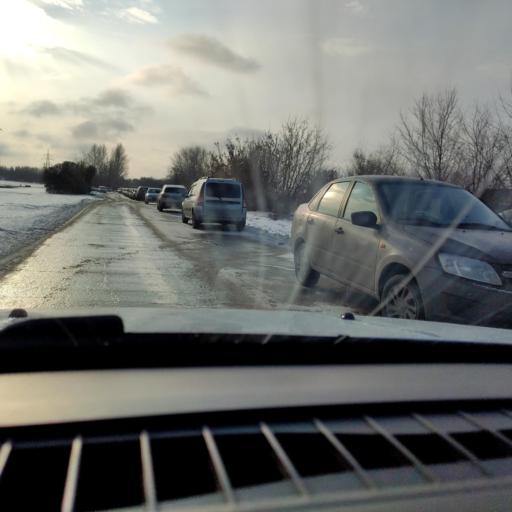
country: RU
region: Samara
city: Tol'yatti
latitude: 53.5571
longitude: 49.2859
